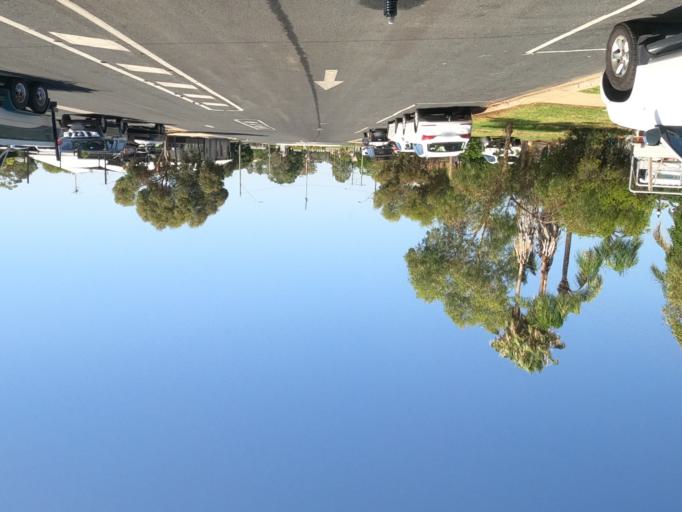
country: AU
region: New South Wales
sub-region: Corowa Shire
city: Mulwala
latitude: -35.9902
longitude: 146.0063
